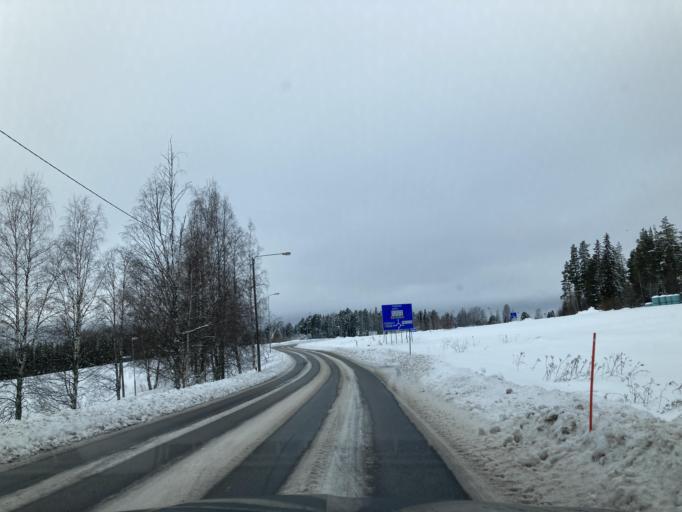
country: FI
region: Central Finland
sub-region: Jaemsae
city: Jaemsae
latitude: 61.8597
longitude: 25.2154
